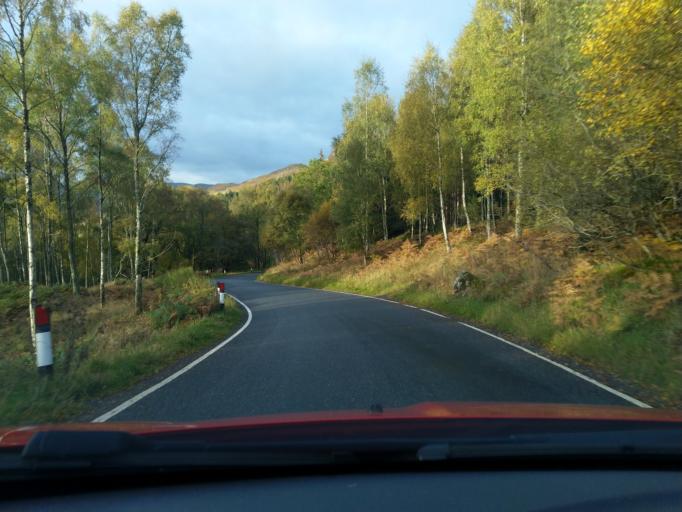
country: GB
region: Scotland
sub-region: Perth and Kinross
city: Aberfeldy
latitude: 56.7185
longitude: -4.1164
